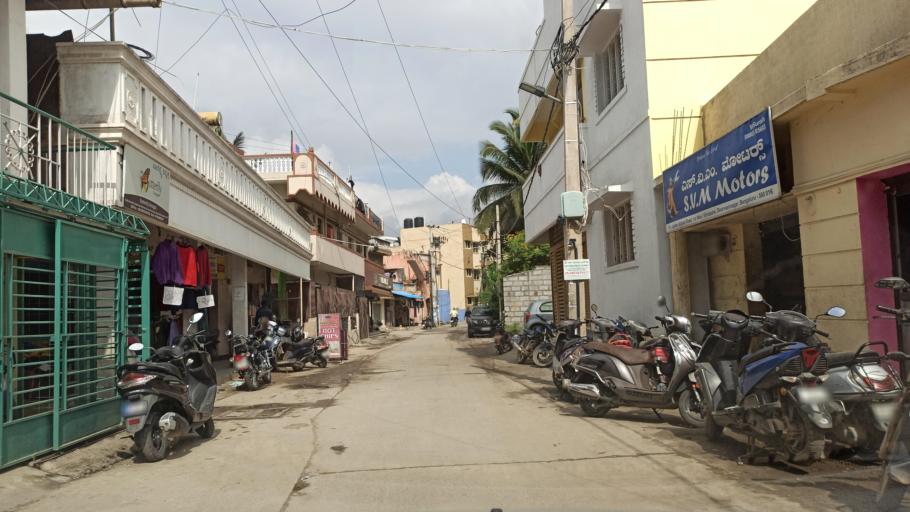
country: IN
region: Karnataka
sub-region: Bangalore Urban
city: Bangalore
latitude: 13.0068
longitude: 77.6744
